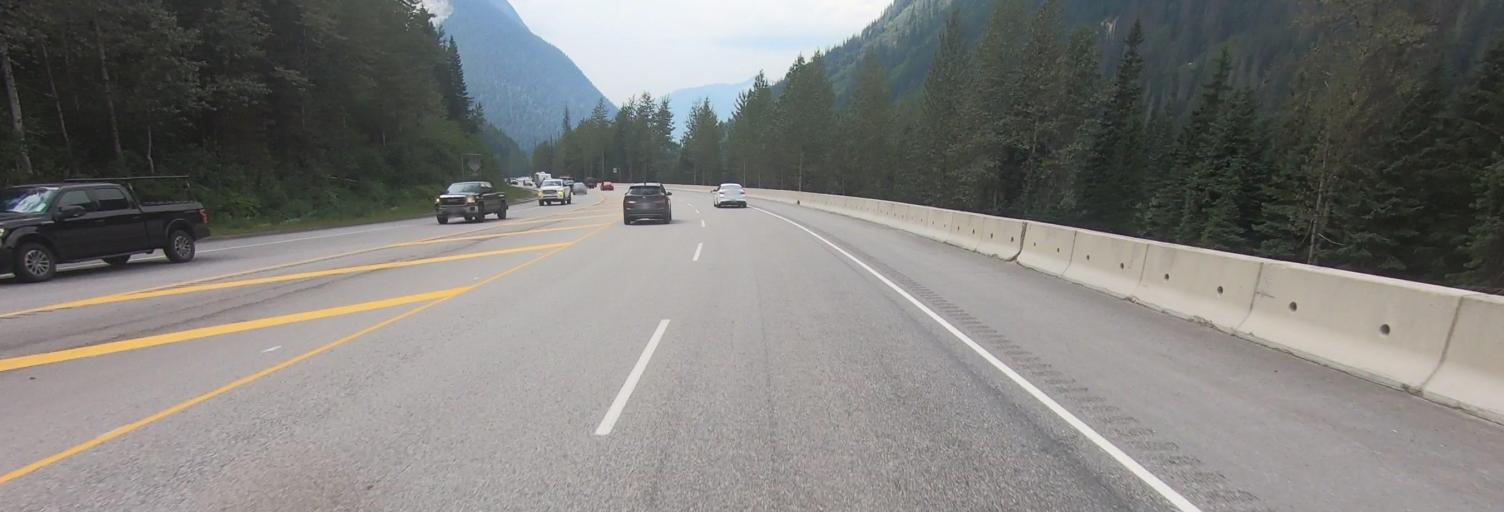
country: CA
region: British Columbia
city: Golden
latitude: 51.2686
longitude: -117.5101
